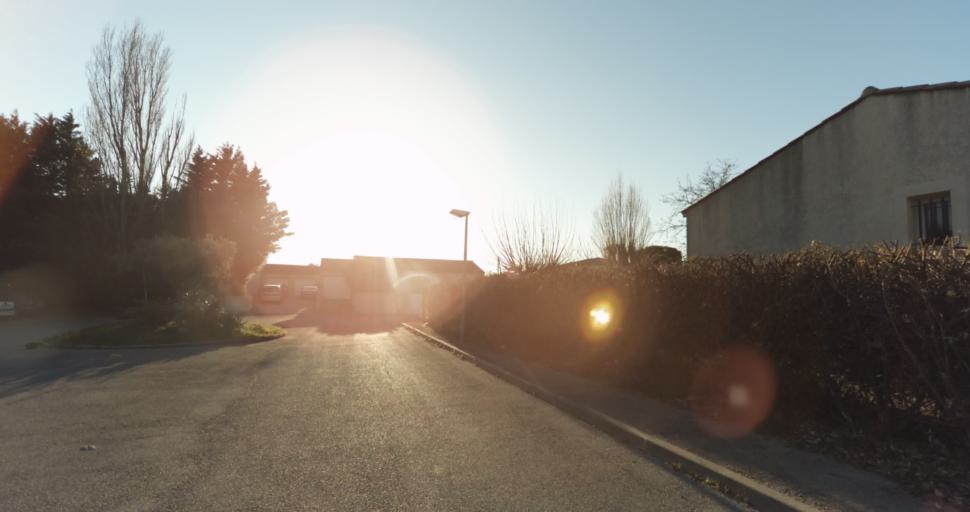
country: FR
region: Provence-Alpes-Cote d'Azur
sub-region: Departement des Bouches-du-Rhone
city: Pelissanne
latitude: 43.6275
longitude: 5.1472
